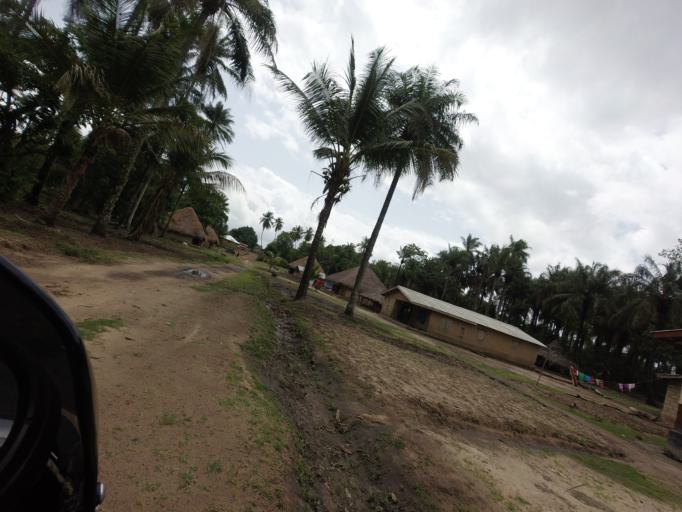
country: SL
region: Northern Province
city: Mambolo
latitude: 8.9947
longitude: -13.0281
